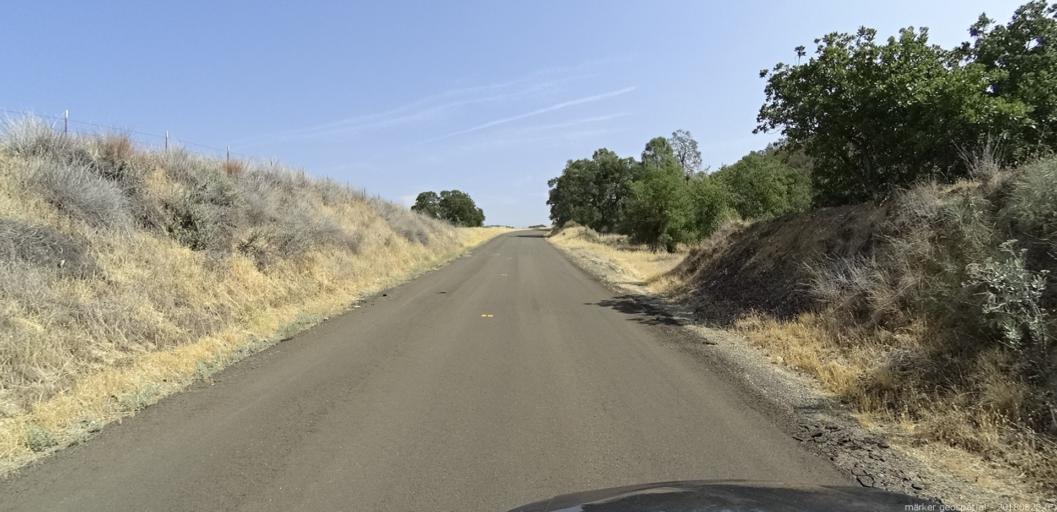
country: US
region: California
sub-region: San Luis Obispo County
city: San Miguel
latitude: 35.9071
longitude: -120.5499
